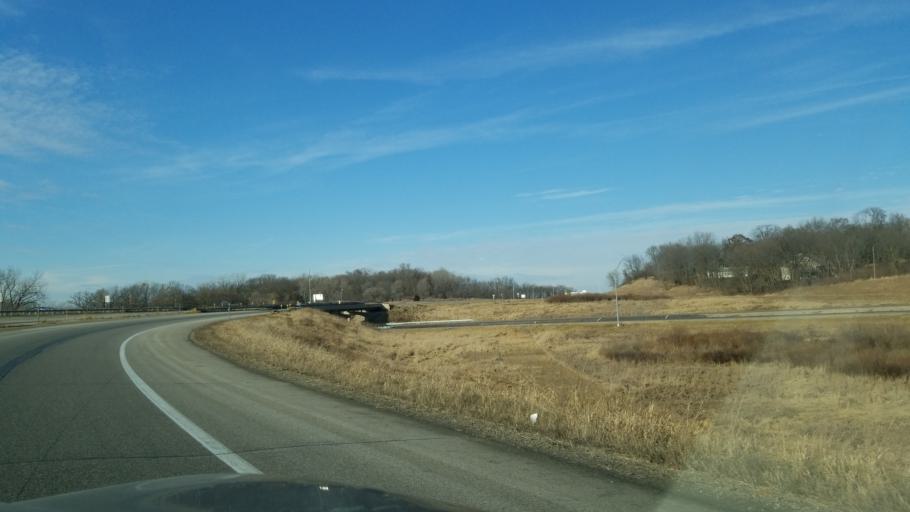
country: US
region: Iowa
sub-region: Linn County
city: Ely
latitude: 41.9249
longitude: -91.5402
